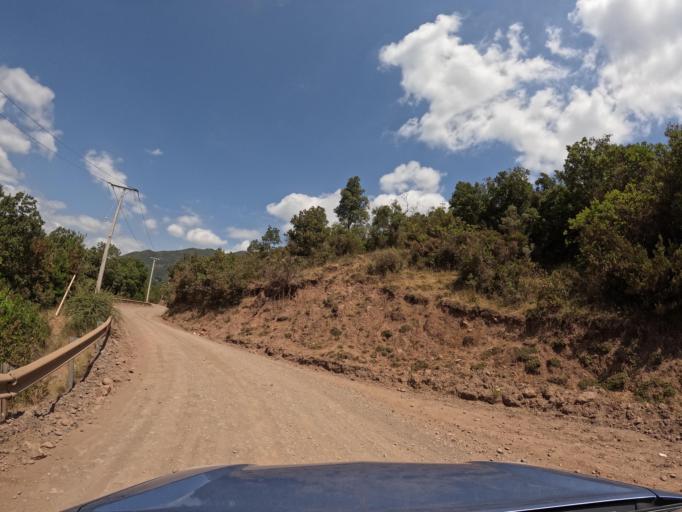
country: CL
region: Maule
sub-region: Provincia de Curico
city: Curico
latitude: -35.1215
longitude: -71.0066
